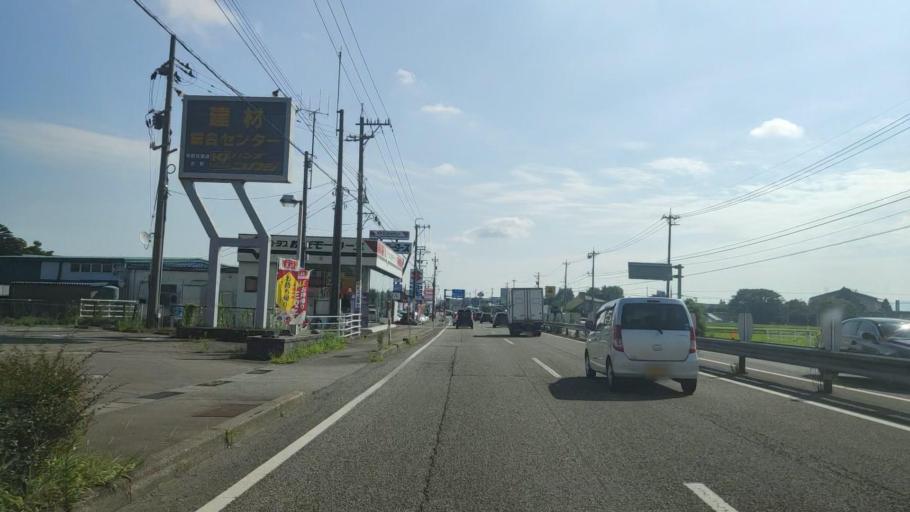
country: JP
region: Ishikawa
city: Matsuto
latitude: 36.5122
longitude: 136.5702
